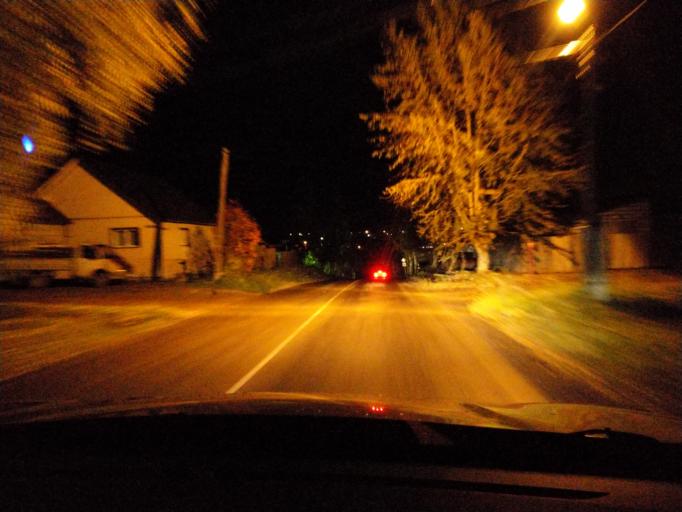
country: RU
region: Perm
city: Dobryanka
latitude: 58.4659
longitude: 56.4184
